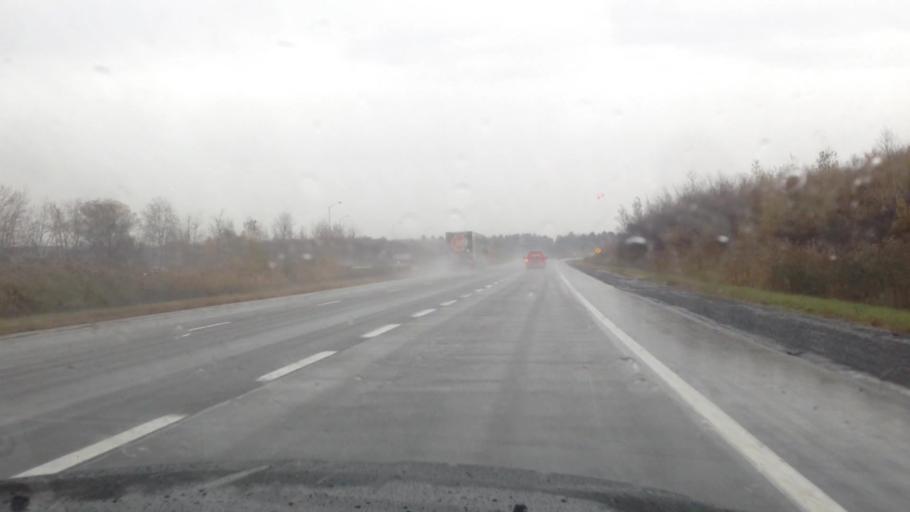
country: CA
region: Ontario
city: Bourget
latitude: 45.3132
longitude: -75.2413
